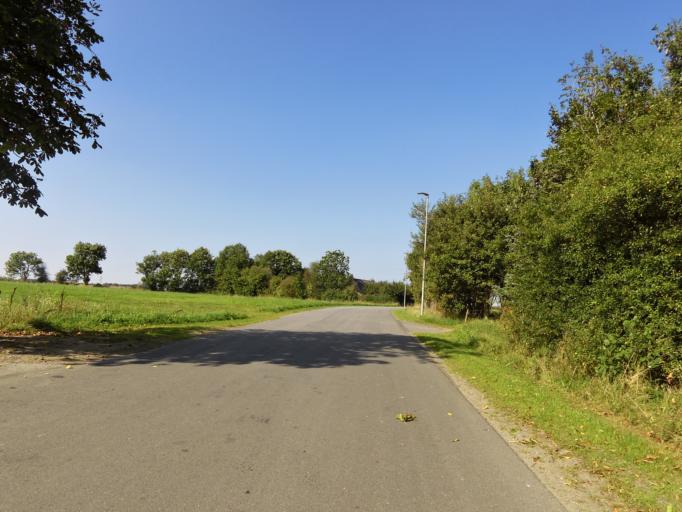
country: DK
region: South Denmark
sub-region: Vejen Kommune
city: Rodding
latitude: 55.3478
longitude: 9.1282
